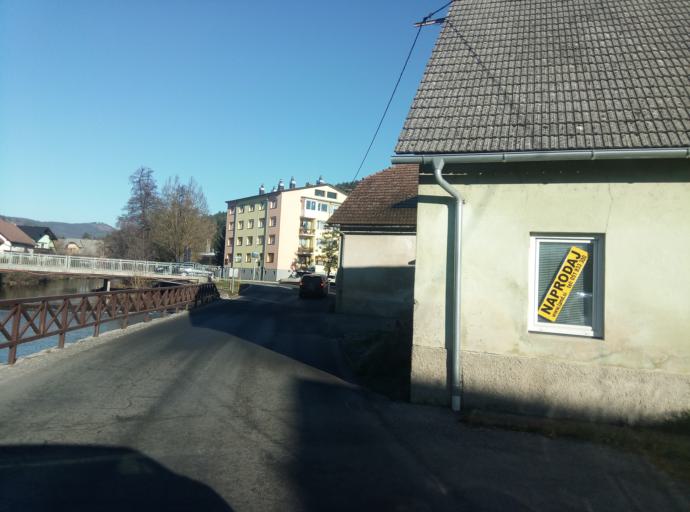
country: SI
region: Cerknica
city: Cerknica
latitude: 45.7928
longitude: 14.3639
